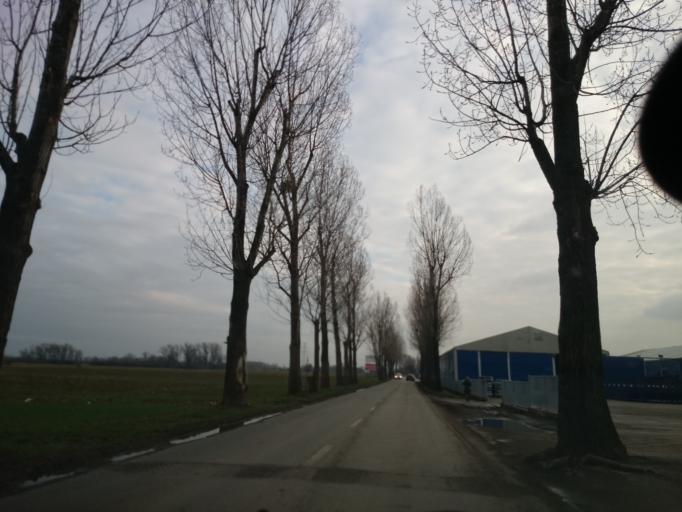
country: PL
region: Opole Voivodeship
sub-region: Powiat opolski
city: Opole
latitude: 50.6534
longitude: 17.9094
